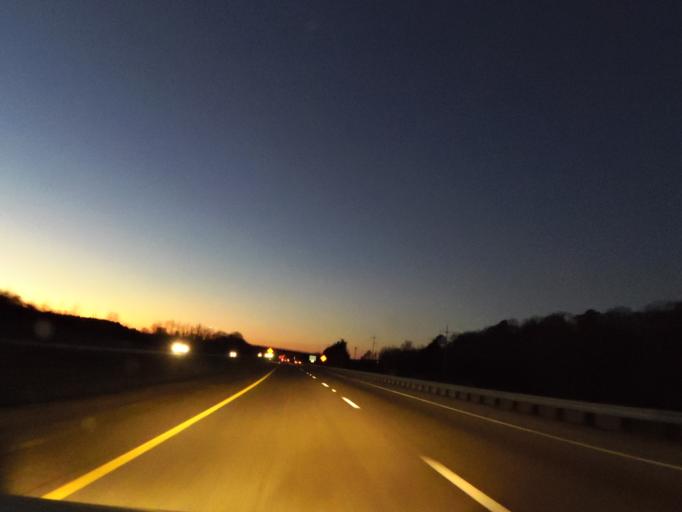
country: US
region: Tennessee
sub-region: Jefferson County
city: White Pine
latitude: 36.0254
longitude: -83.3039
